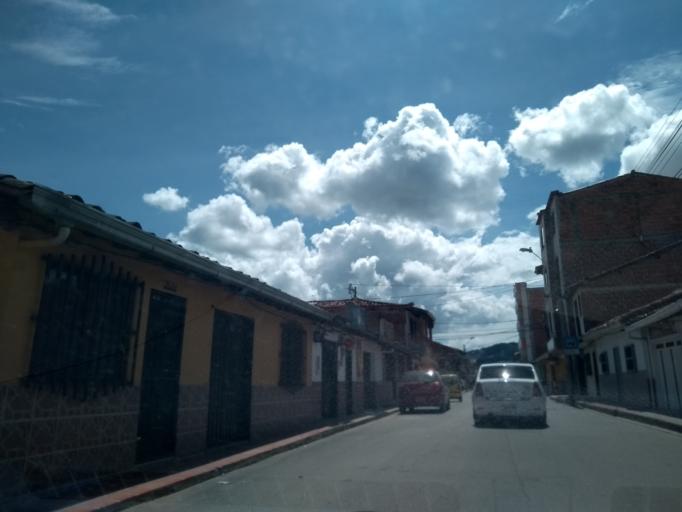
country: CO
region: Antioquia
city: La Ceja
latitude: 6.0347
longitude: -75.4273
